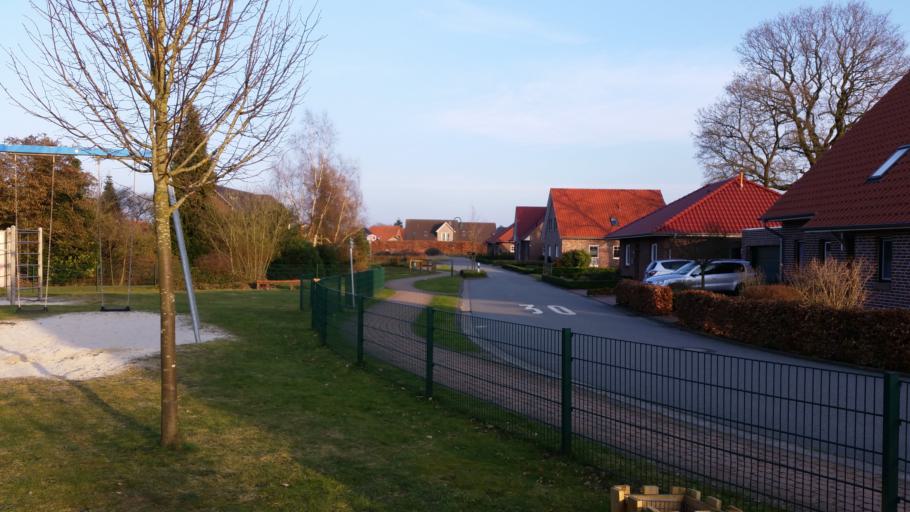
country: DE
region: Lower Saxony
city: Zetel
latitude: 53.4150
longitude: 7.9617
